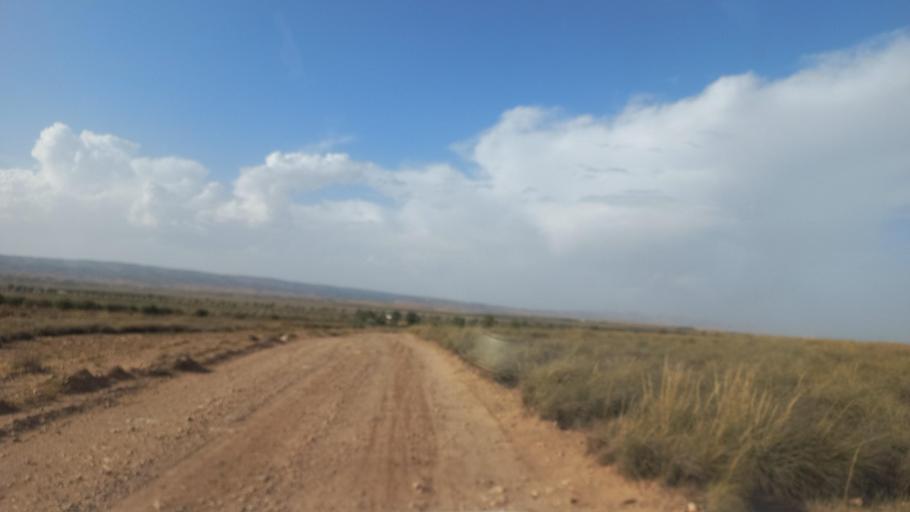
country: TN
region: Al Qasrayn
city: Kasserine
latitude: 35.2200
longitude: 8.9698
